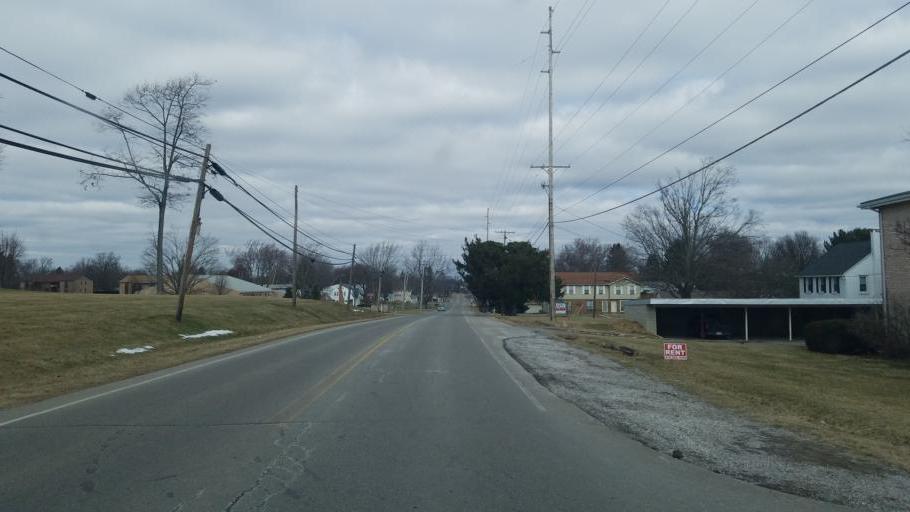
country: US
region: Ohio
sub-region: Richland County
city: Mansfield
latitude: 40.7293
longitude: -82.5131
